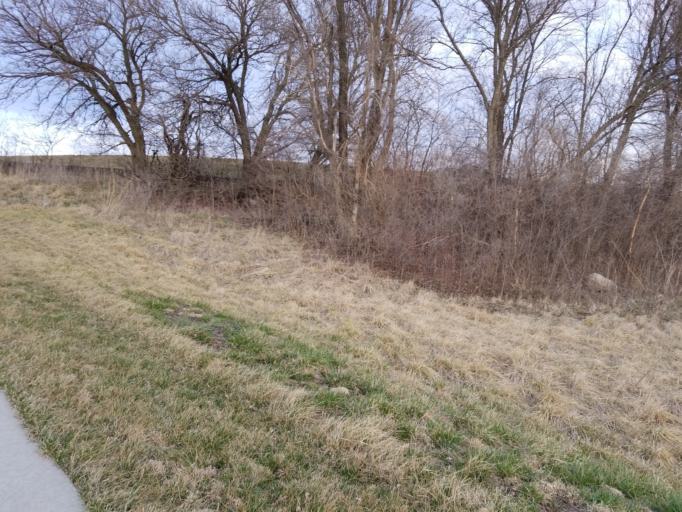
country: US
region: Nebraska
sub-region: Sarpy County
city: Chalco
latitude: 41.1540
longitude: -96.1132
